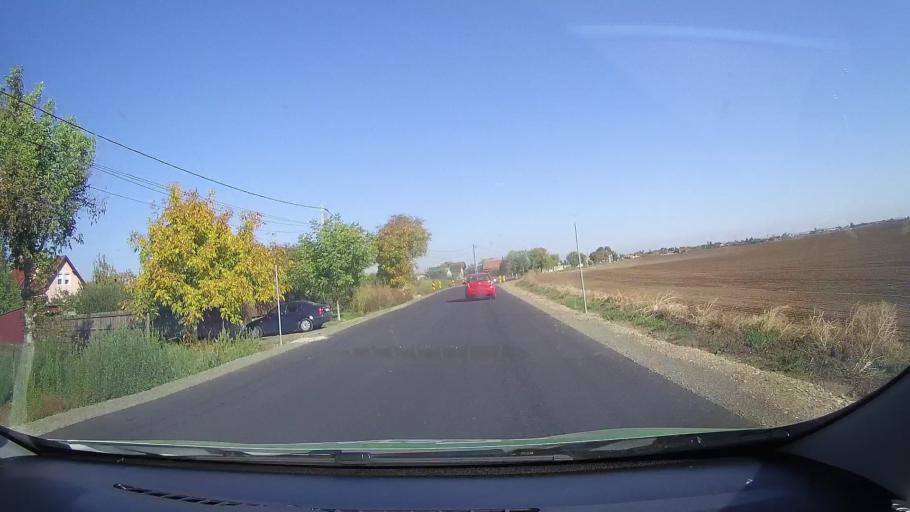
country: RO
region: Satu Mare
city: Carei
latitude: 47.6658
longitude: 22.4614
